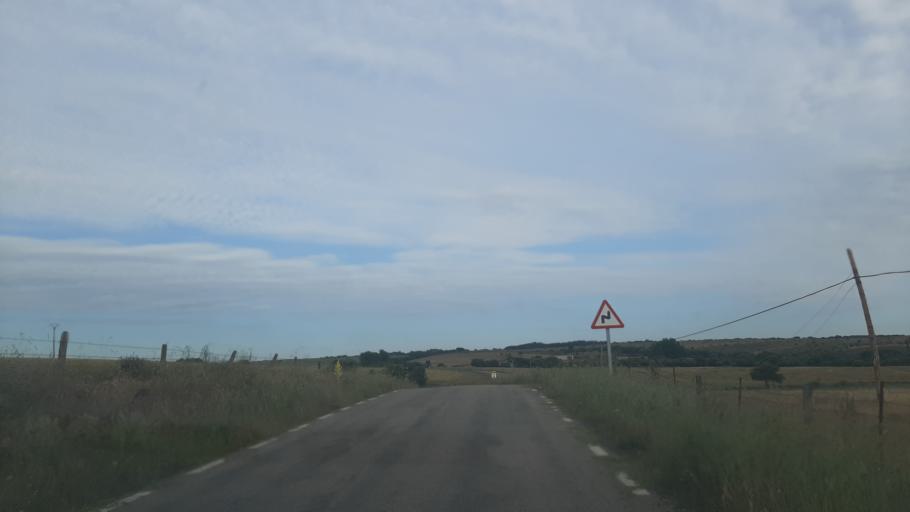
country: ES
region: Castille and Leon
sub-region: Provincia de Salamanca
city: Gallegos de Arganan
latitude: 40.6354
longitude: -6.7152
